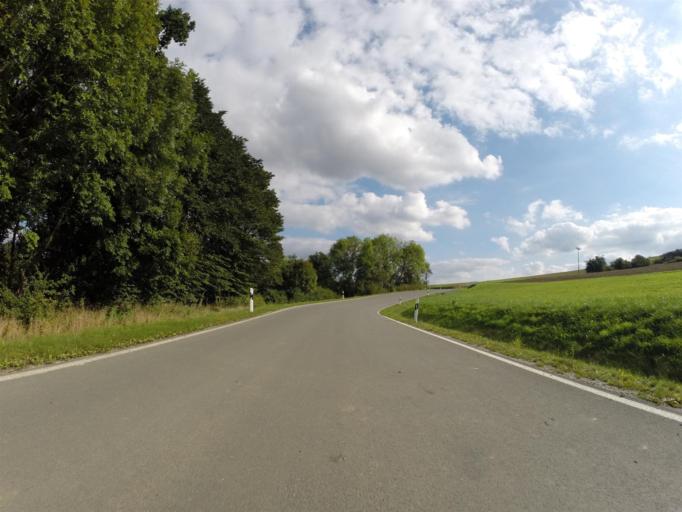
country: DE
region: Thuringia
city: Rothenstein
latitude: 50.8678
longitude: 11.5863
